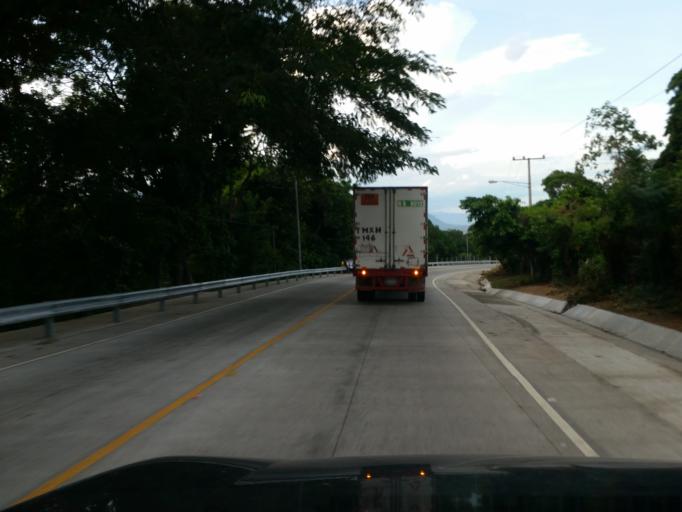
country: NI
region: Managua
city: Ciudad Sandino
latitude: 12.0840
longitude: -86.3603
